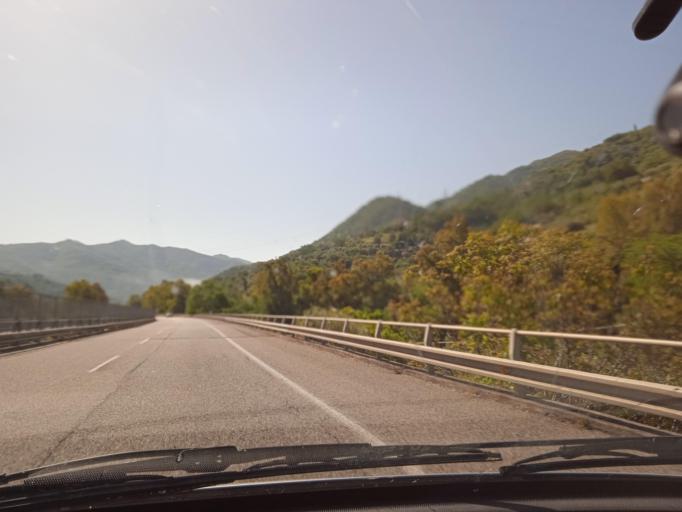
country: IT
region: Sicily
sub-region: Messina
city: Gliaca
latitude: 38.1520
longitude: 14.8483
